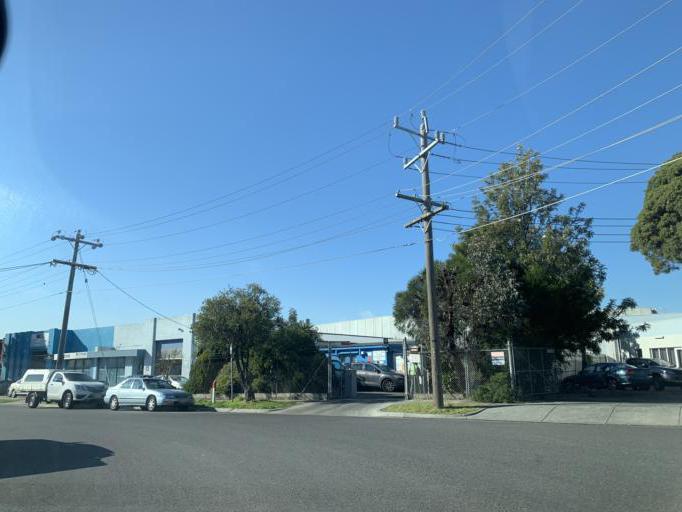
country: AU
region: Victoria
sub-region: Greater Dandenong
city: Dandenong
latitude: -37.9862
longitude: 145.1891
